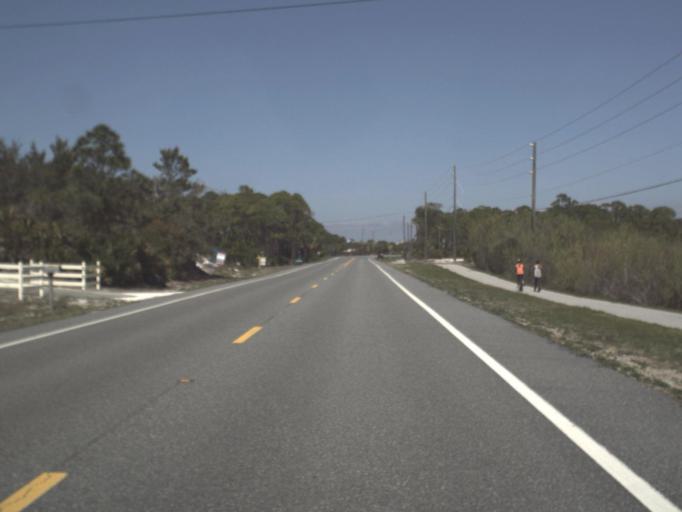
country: US
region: Florida
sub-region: Gulf County
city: Port Saint Joe
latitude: 29.7398
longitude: -85.3944
